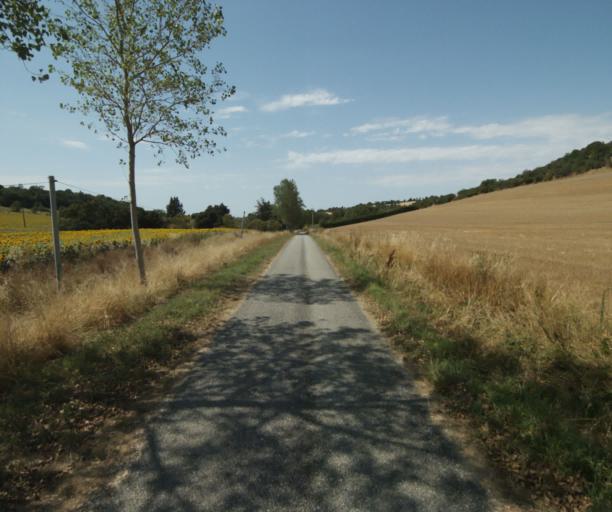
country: FR
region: Midi-Pyrenees
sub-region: Departement de la Haute-Garonne
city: Saint-Felix-Lauragais
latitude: 43.4536
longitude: 1.8842
